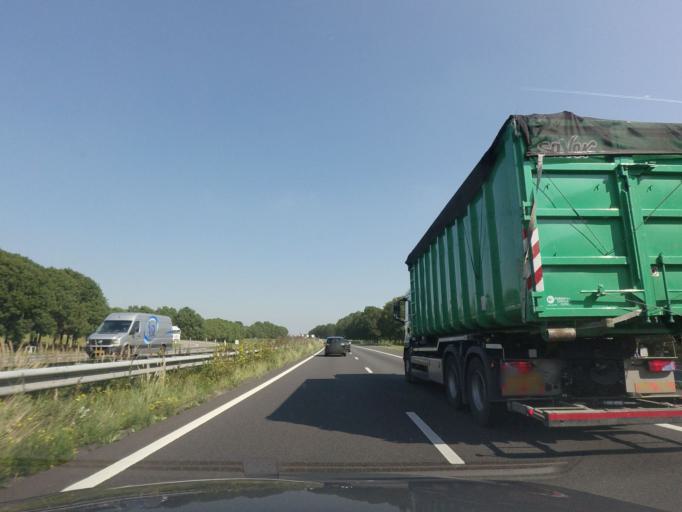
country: NL
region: North Brabant
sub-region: Gemeente Moerdijk
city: Klundert
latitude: 51.6717
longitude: 4.6099
